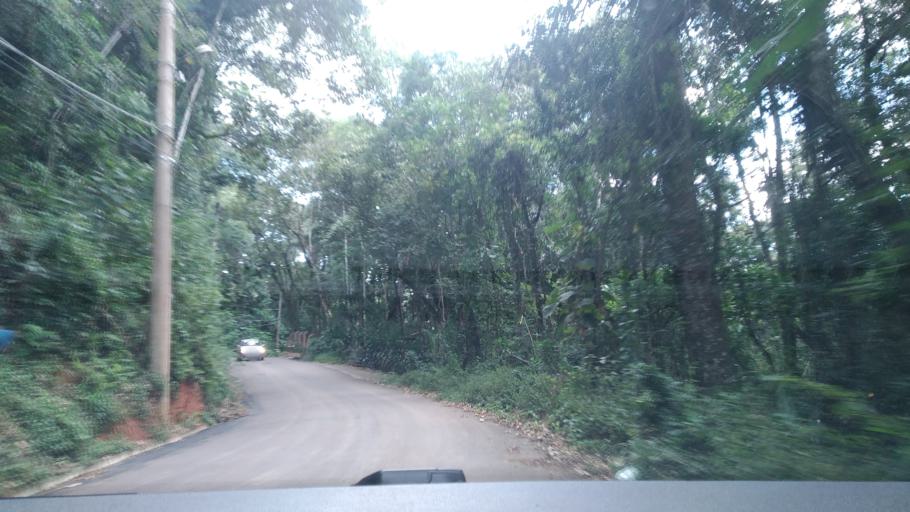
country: BR
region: Sao Paulo
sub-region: Cajamar
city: Cajamar
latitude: -23.2815
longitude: -46.8956
